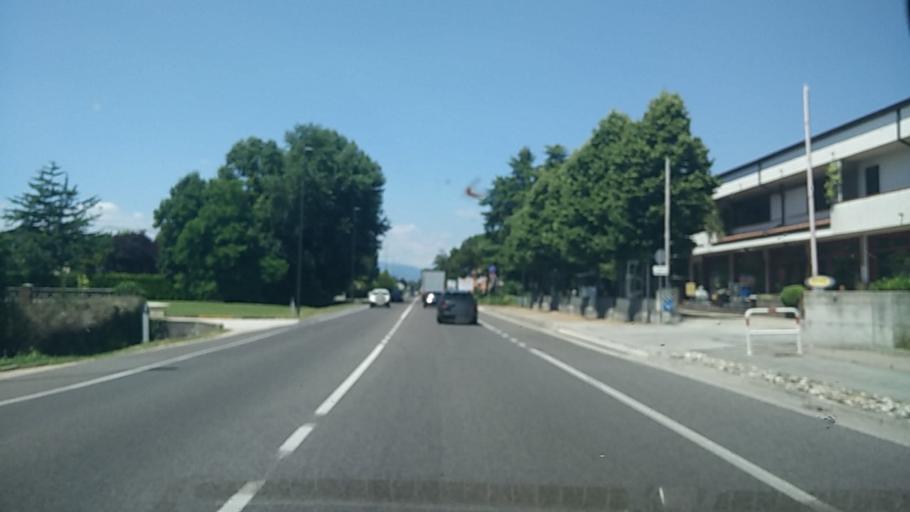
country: IT
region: Veneto
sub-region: Provincia di Padova
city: San Giorgio in Bosco
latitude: 45.5944
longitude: 11.8052
